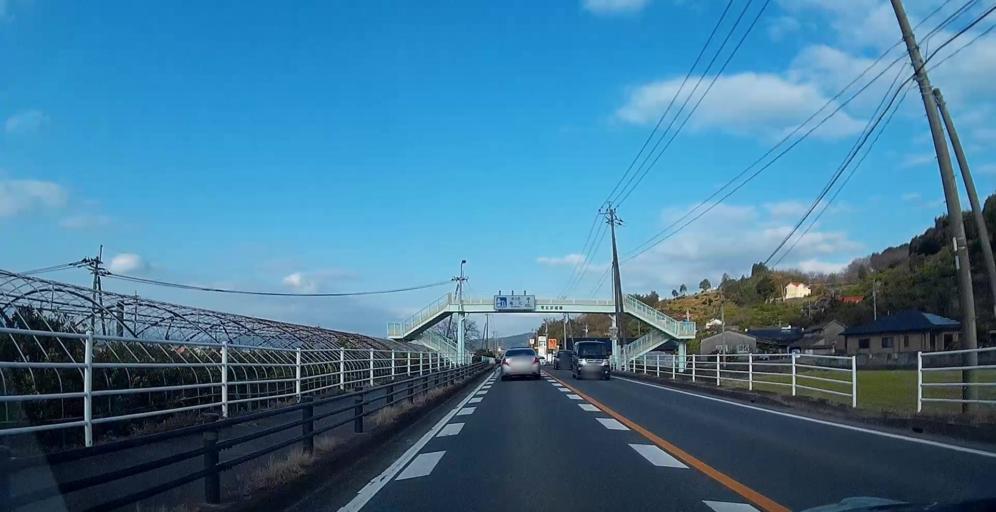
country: JP
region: Kumamoto
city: Matsubase
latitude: 32.5732
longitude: 130.6929
